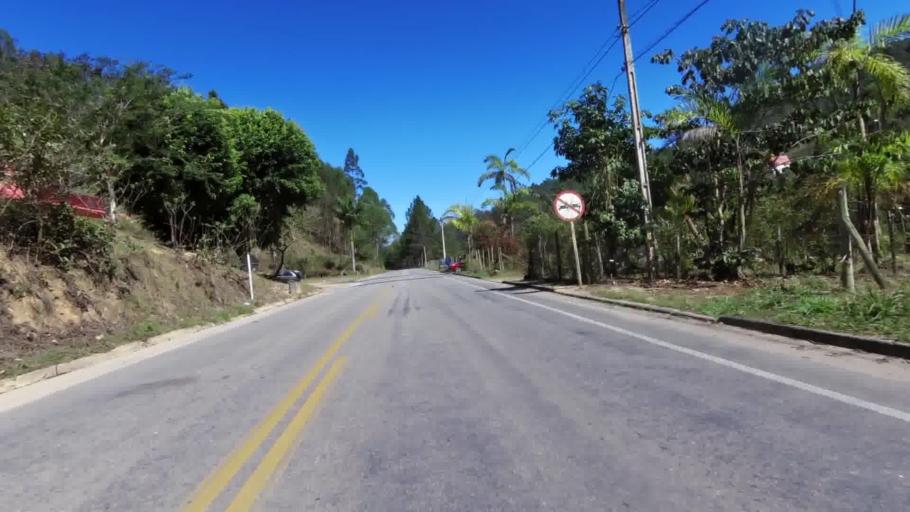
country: BR
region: Espirito Santo
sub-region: Vargem Alta
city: Vargem Alta
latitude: -20.6605
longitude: -40.9759
